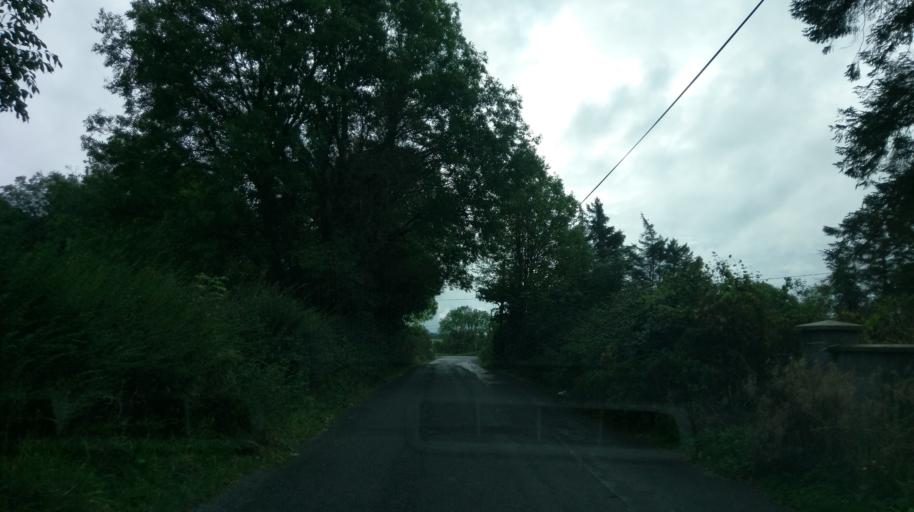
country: IE
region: Connaught
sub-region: County Galway
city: Athenry
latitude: 53.4439
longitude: -8.5647
